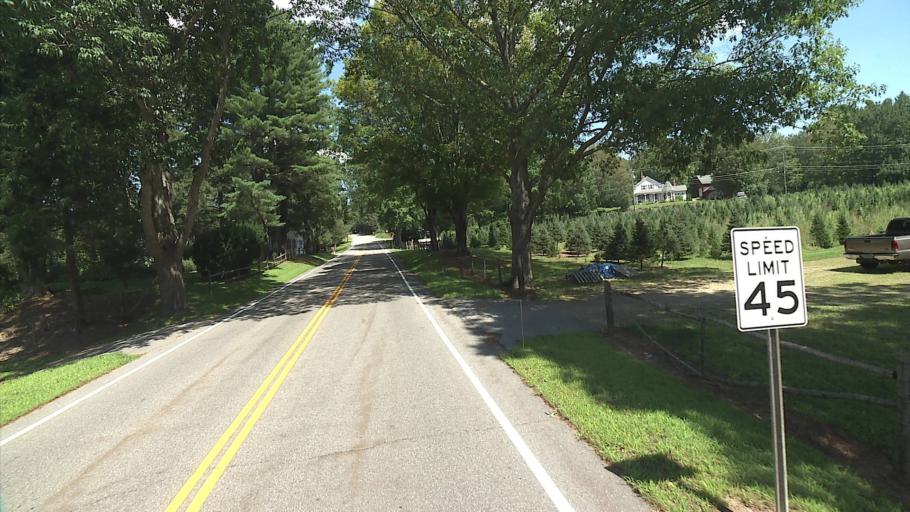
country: US
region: Connecticut
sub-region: Windham County
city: South Woodstock
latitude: 41.9410
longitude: -72.0737
